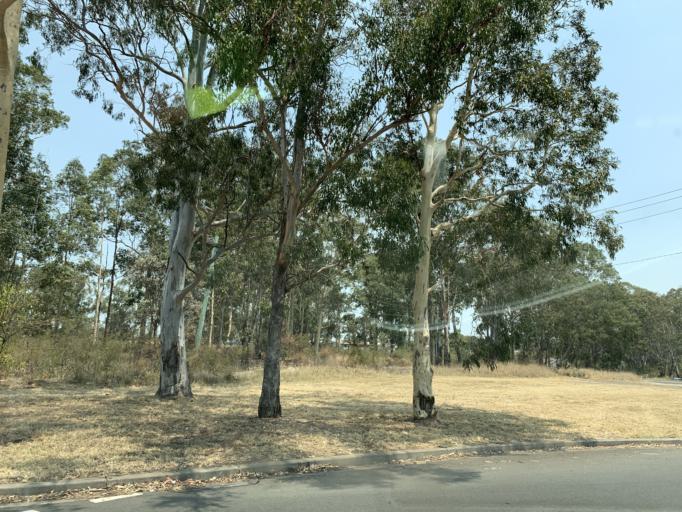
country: AU
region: New South Wales
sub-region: Fairfield
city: Horsley Park
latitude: -33.8344
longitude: 150.8735
